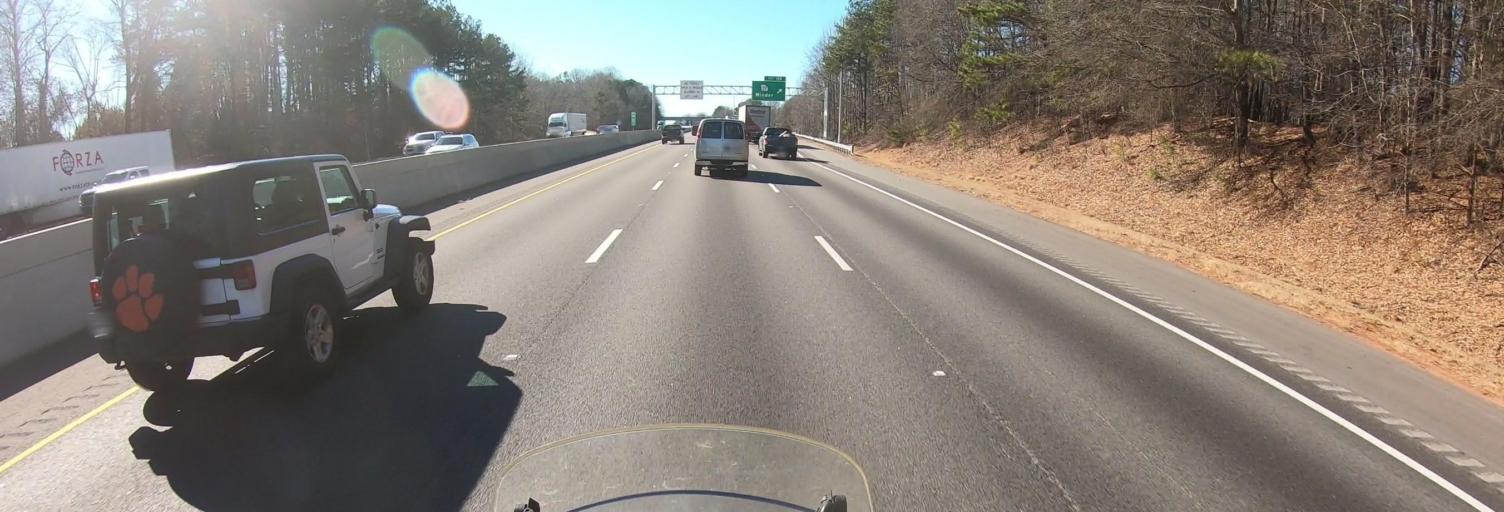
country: US
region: Georgia
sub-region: Jackson County
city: Braselton
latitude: 34.0984
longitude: -83.8061
